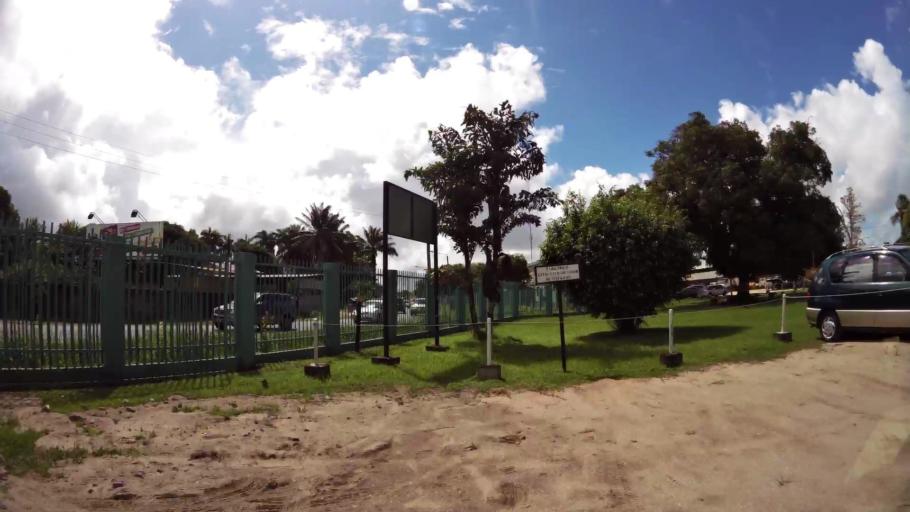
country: SR
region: Paramaribo
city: Paramaribo
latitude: 5.8312
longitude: -55.1865
